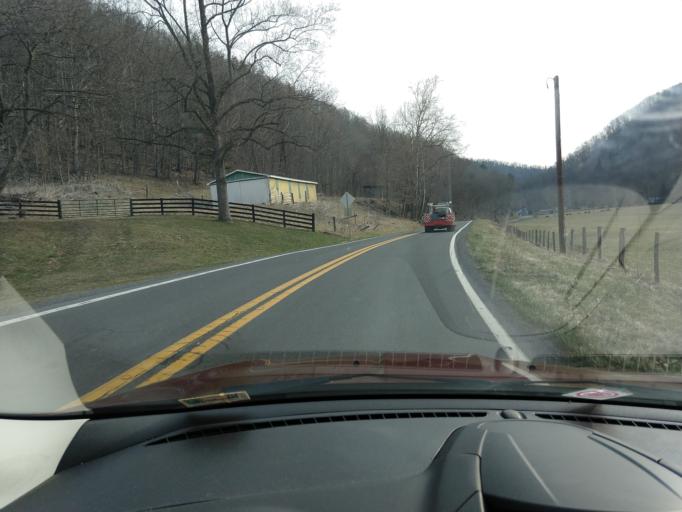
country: US
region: West Virginia
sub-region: Pendleton County
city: Franklin
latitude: 38.5977
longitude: -79.3853
